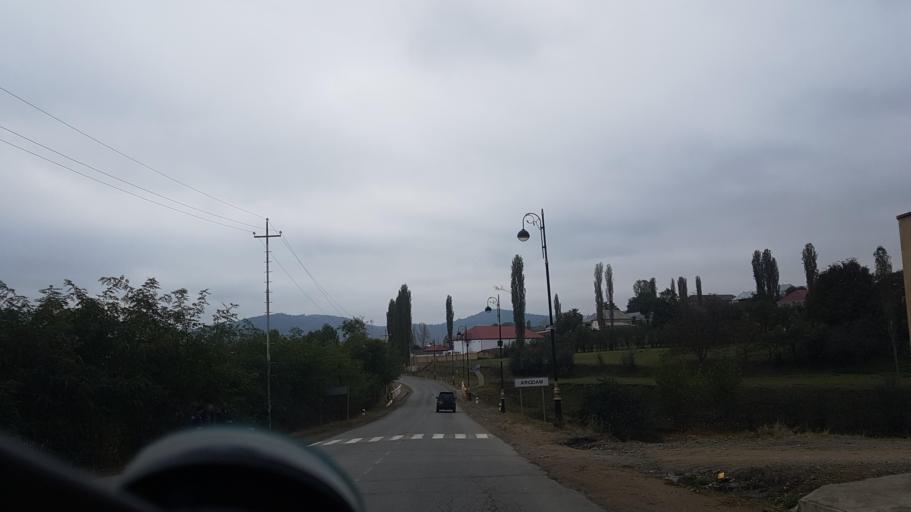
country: AZ
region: Gadabay Rayon
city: Ariqdam
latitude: 40.5954
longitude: 45.8107
